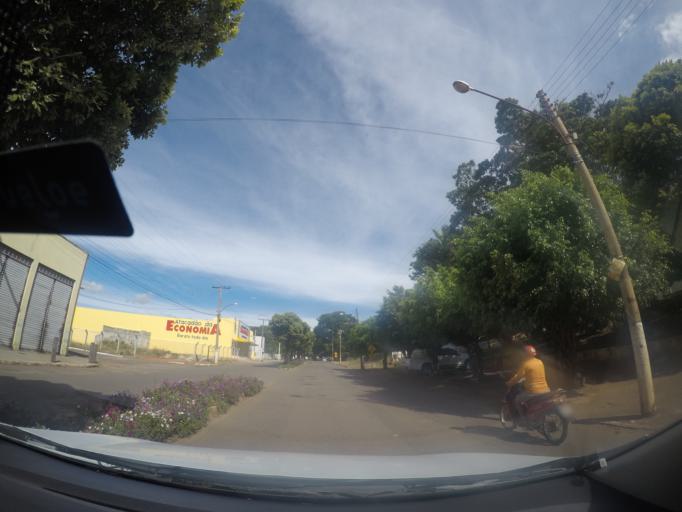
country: BR
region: Goias
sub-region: Inhumas
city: Inhumas
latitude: -16.3670
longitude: -49.4971
